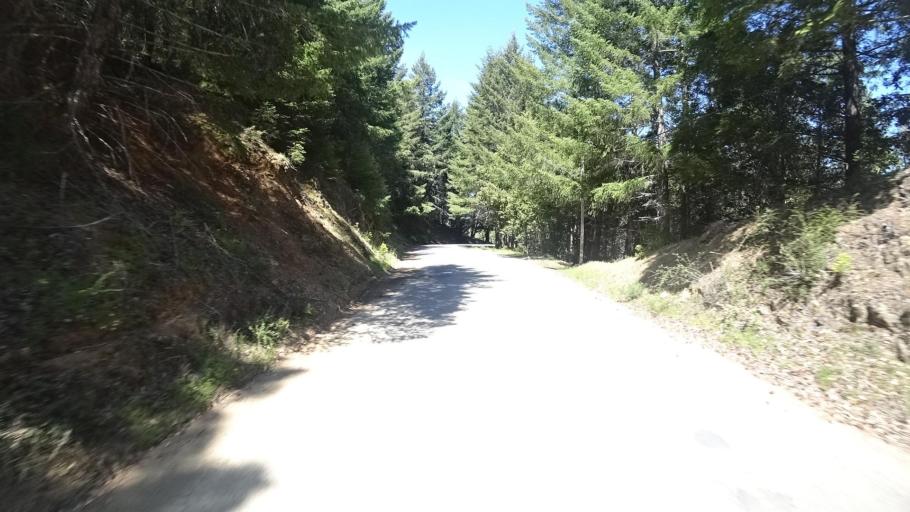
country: US
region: California
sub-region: Humboldt County
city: Redway
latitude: 40.1250
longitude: -123.9722
